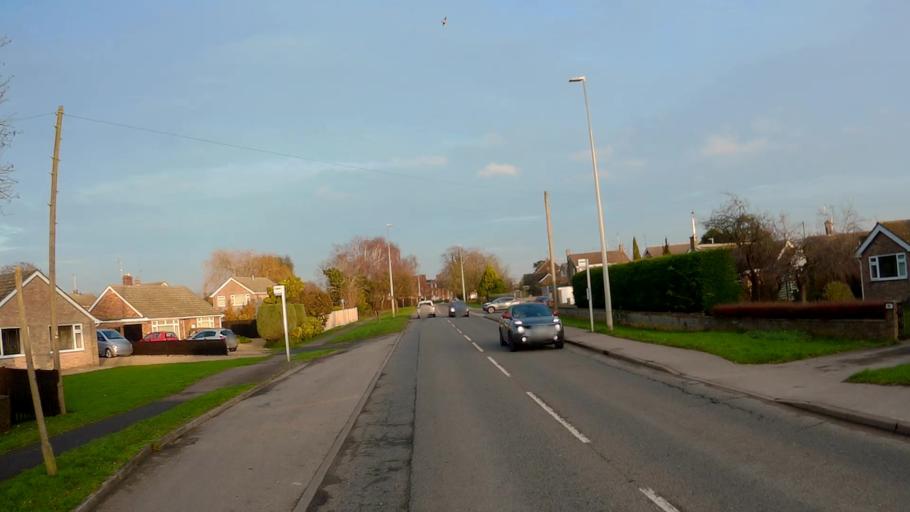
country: GB
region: England
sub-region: Lincolnshire
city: Bourne
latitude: 52.7666
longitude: -0.3921
